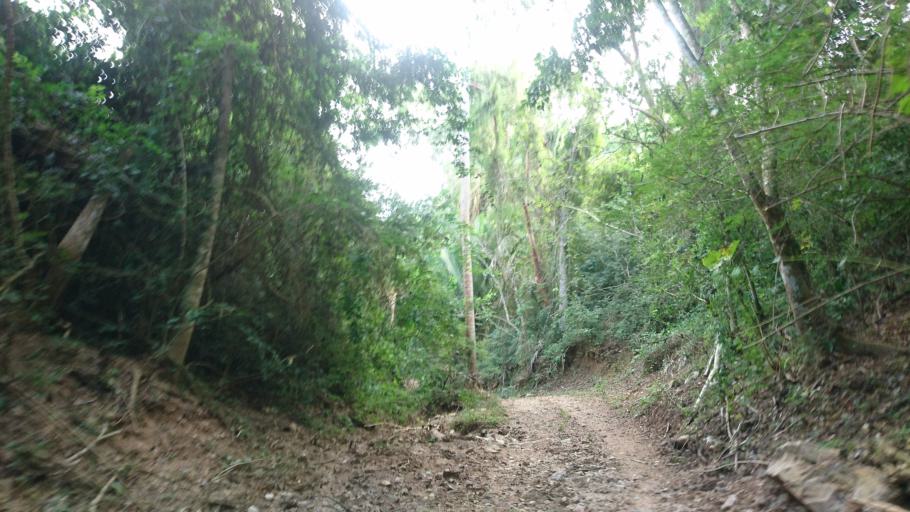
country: MX
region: Nayarit
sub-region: Bahia de Banderas
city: Corral del Risco (Punta de Mita)
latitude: 20.8280
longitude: -105.4629
